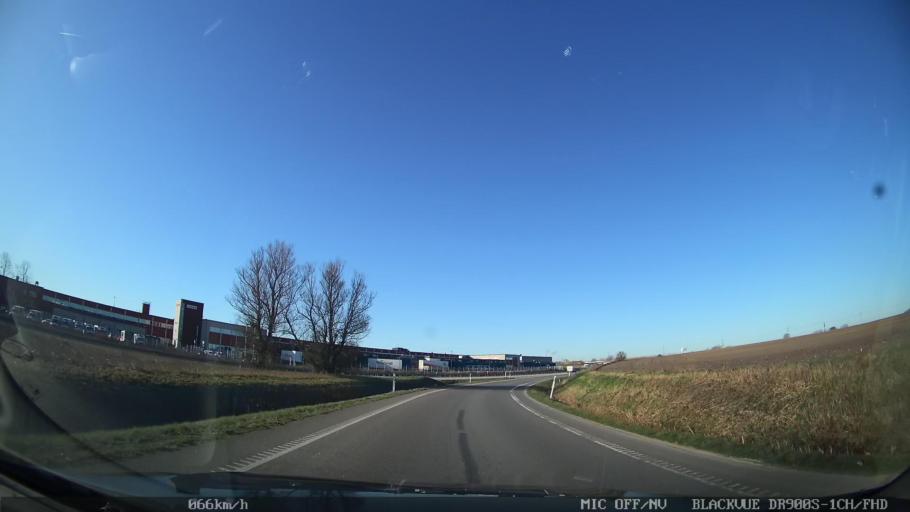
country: SE
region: Skane
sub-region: Burlovs Kommun
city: Arloev
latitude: 55.6478
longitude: 13.0777
